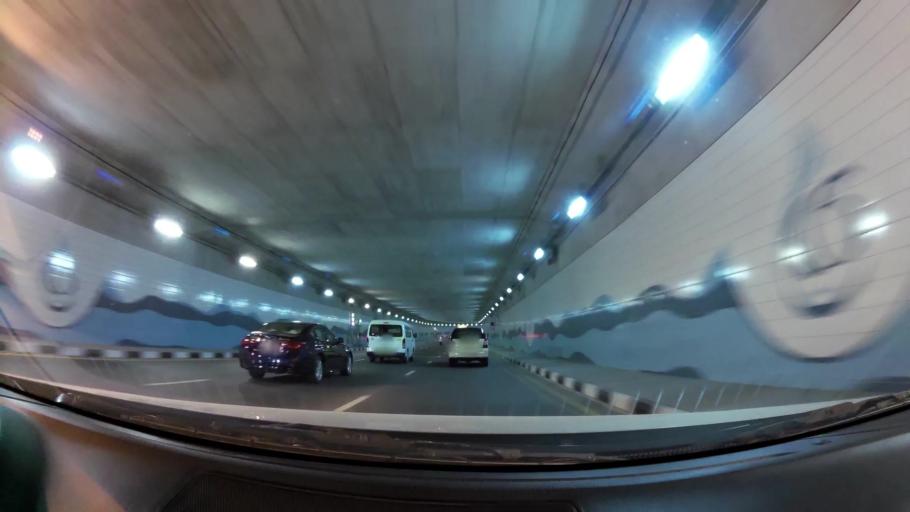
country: AE
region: Dubai
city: Dubai
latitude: 25.1253
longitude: 55.1189
